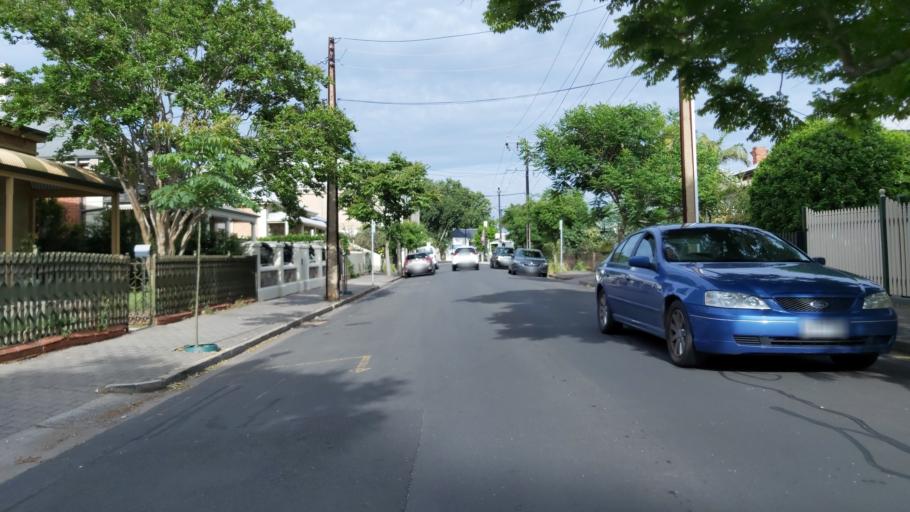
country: AU
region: South Australia
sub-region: Unley
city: Millswood
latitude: -34.9527
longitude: 138.5911
